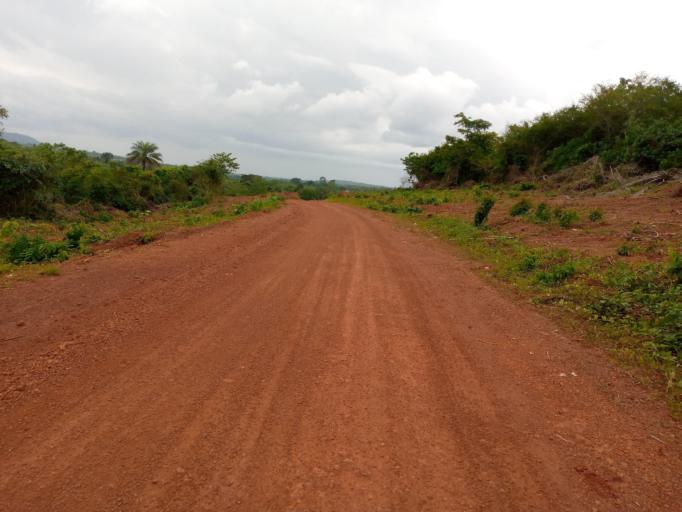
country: SL
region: Southern Province
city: Moyamba
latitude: 8.0767
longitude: -12.4536
